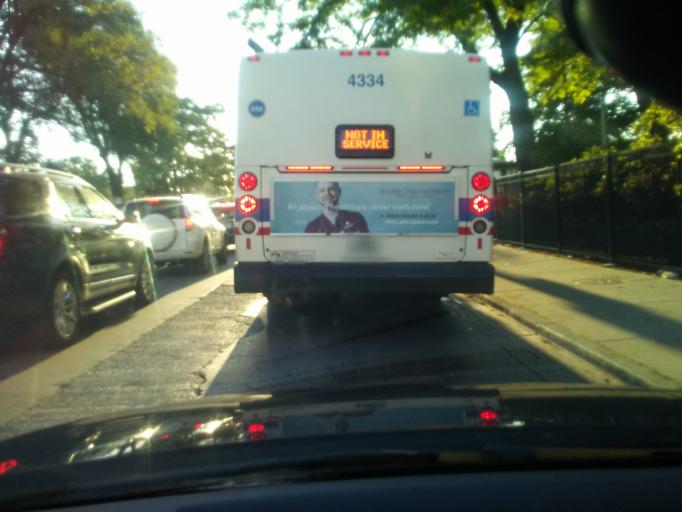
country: US
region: Illinois
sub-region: Cook County
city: Evanston
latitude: 41.9764
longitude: -87.6526
